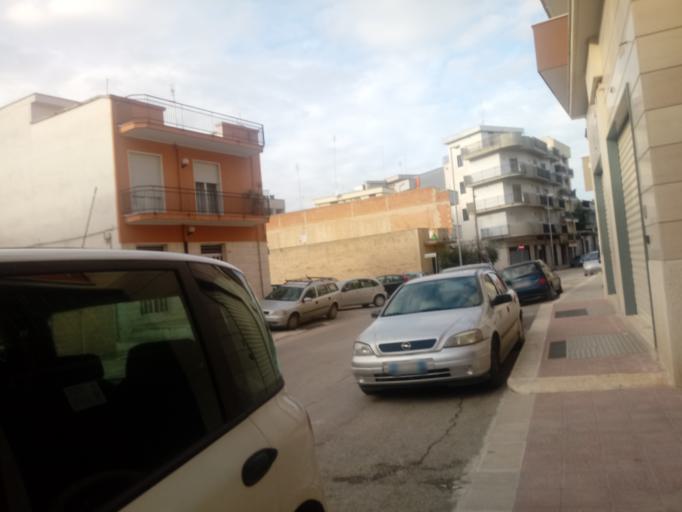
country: IT
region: Apulia
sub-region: Provincia di Barletta - Andria - Trani
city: Andria
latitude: 41.2167
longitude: 16.2958
